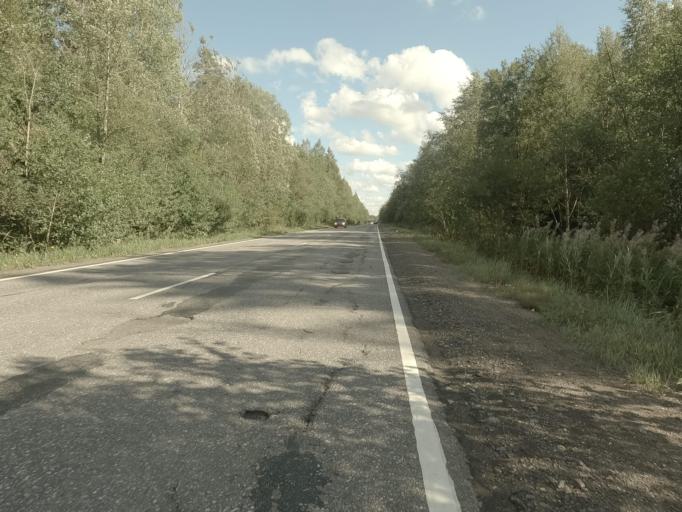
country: RU
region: Leningrad
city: Shcheglovo
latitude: 59.9952
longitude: 30.8777
